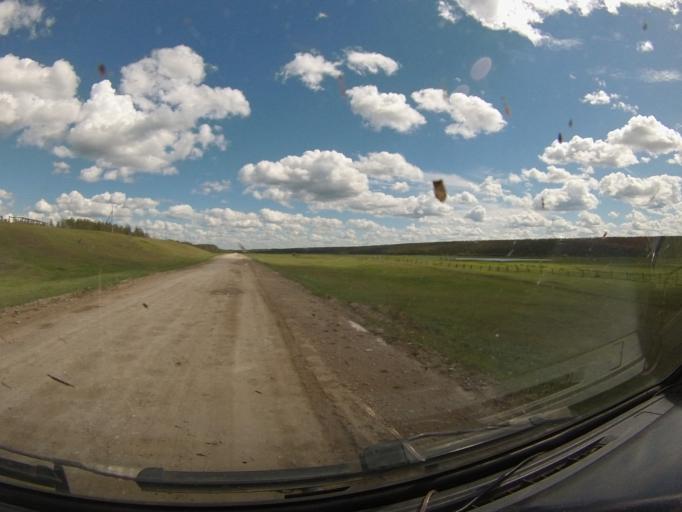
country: RU
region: Sakha
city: Borogontsy
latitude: 62.1423
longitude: 131.1704
